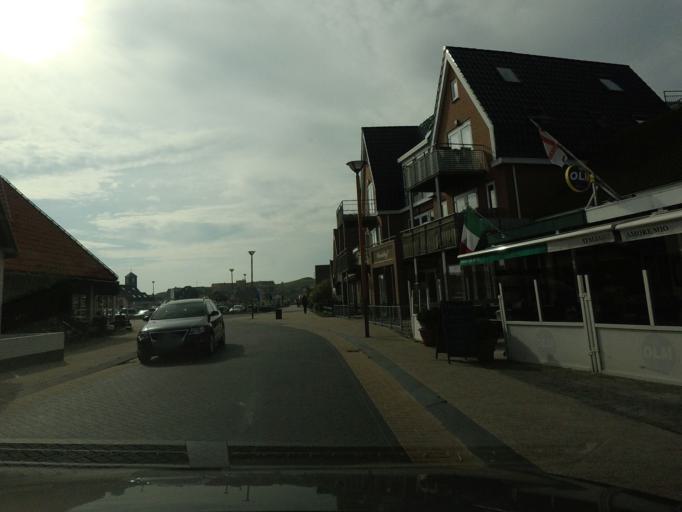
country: NL
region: North Holland
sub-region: Gemeente Schagen
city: Schagen
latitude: 52.8366
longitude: 4.6954
